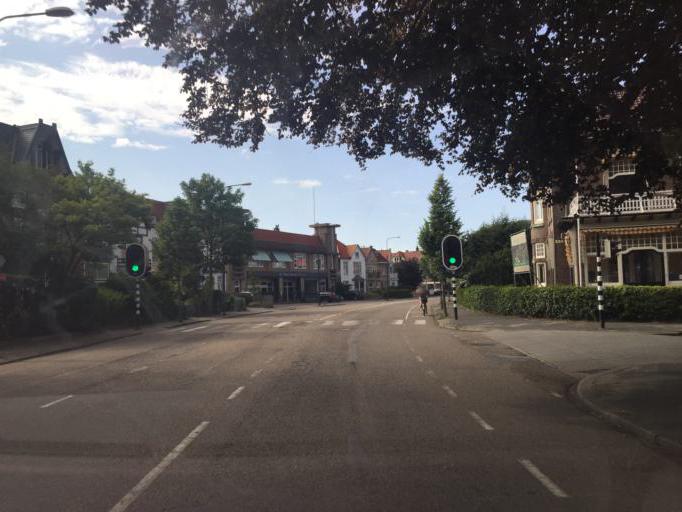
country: NL
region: South Holland
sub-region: Gemeente Oegstgeest
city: Oegstgeest
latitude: 52.1779
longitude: 4.4663
